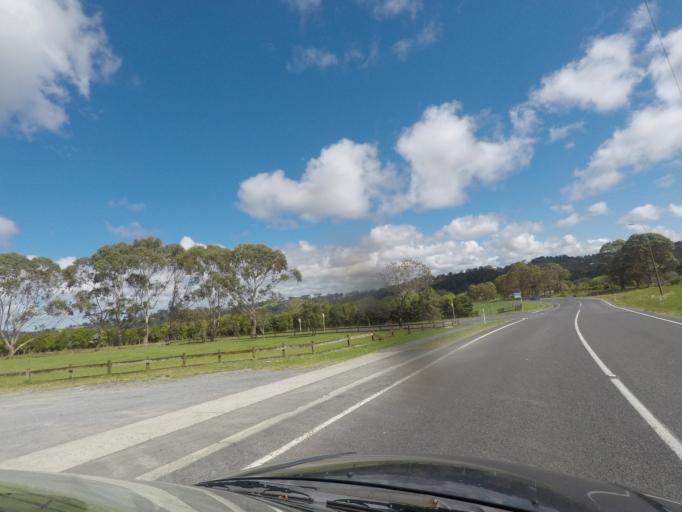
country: NZ
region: Auckland
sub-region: Auckland
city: Rothesay Bay
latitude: -36.7578
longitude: 174.6501
